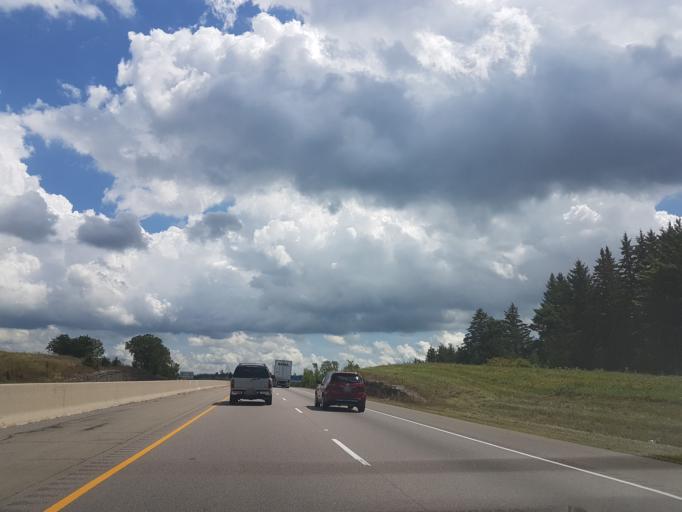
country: CA
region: Ontario
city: Belleville
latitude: 44.2193
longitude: -77.2734
